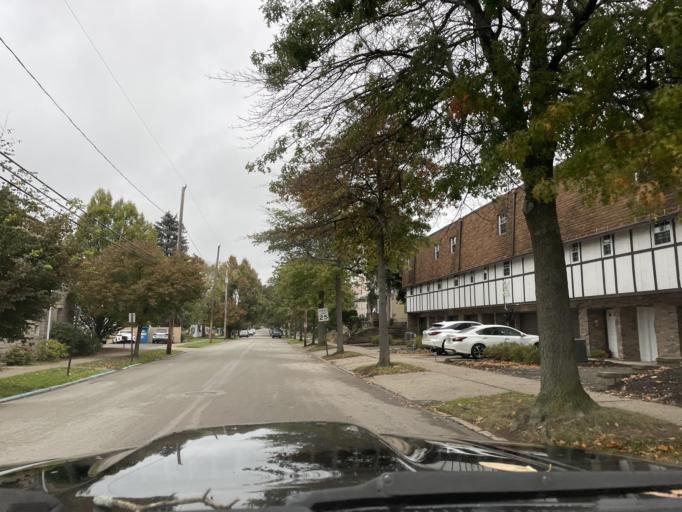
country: US
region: Pennsylvania
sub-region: Allegheny County
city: Oakmont
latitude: 40.5188
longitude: -79.8392
